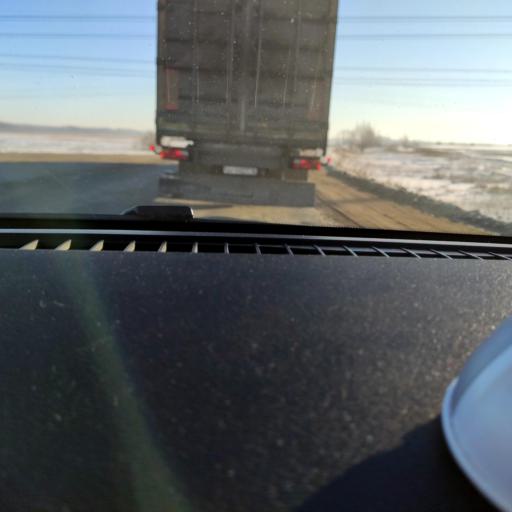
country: RU
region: Samara
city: Spiridonovka
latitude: 53.1424
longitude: 50.5943
